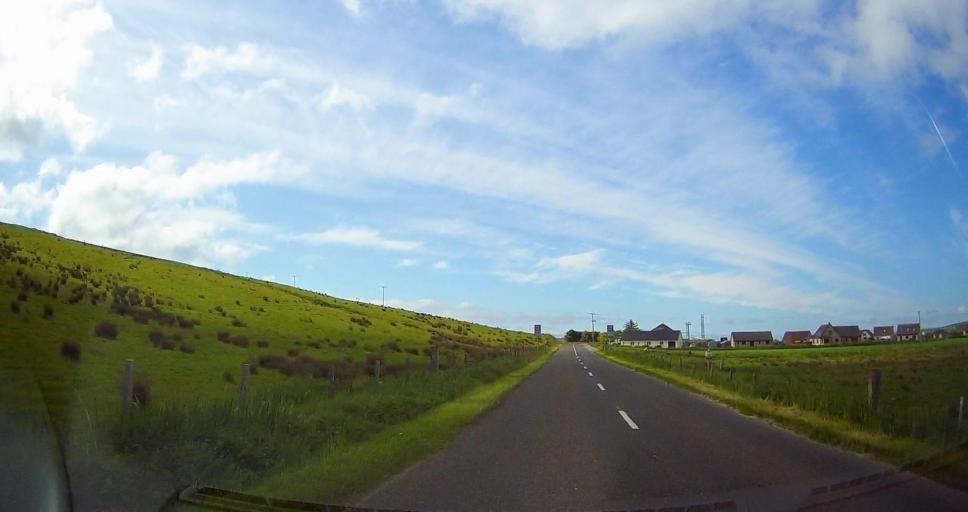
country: GB
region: Scotland
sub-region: Orkney Islands
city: Orkney
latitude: 58.9640
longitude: -2.9667
